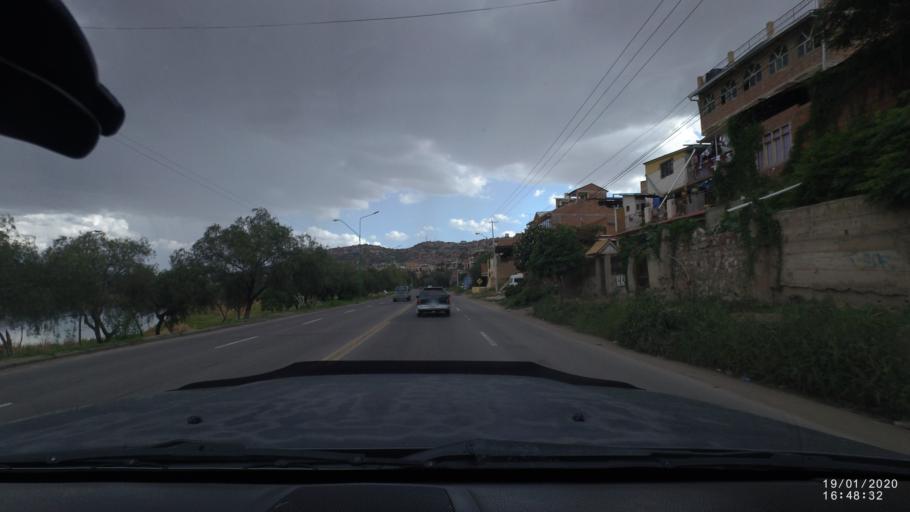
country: BO
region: Cochabamba
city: Cochabamba
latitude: -17.4112
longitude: -66.1425
